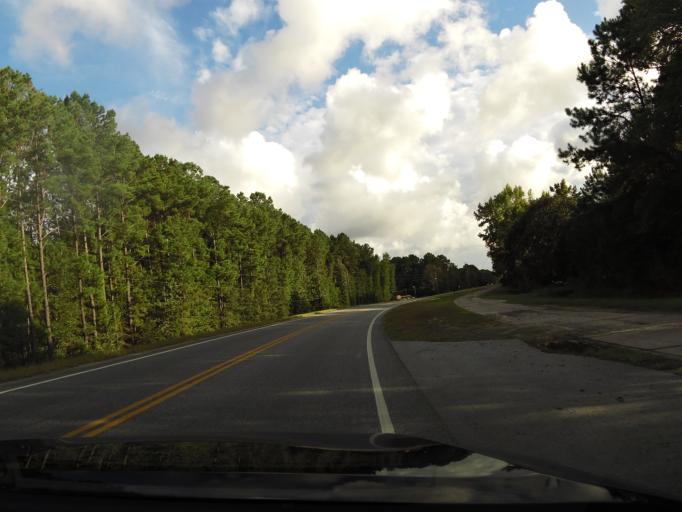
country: US
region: Georgia
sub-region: Liberty County
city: Midway
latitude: 31.7197
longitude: -81.4169
